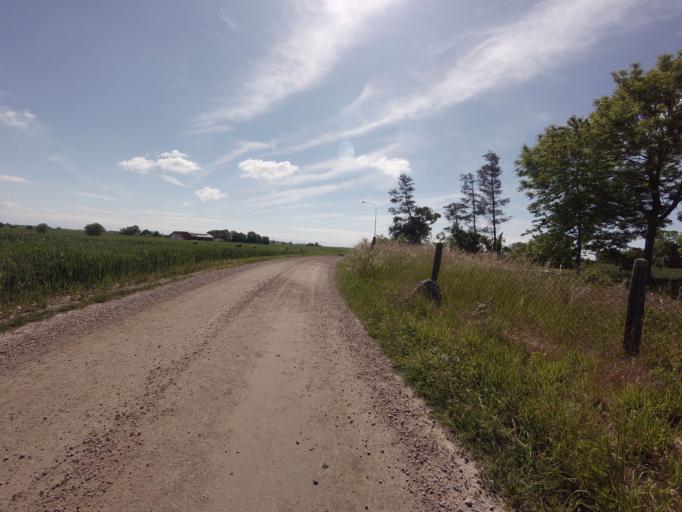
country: SE
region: Skane
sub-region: Trelleborgs Kommun
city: Skare
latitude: 55.4180
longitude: 13.0332
